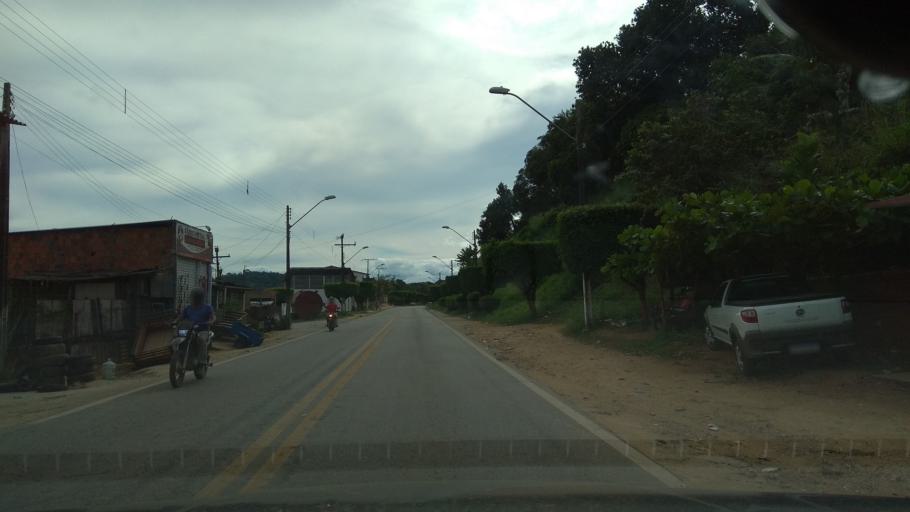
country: BR
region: Bahia
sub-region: Ubata
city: Ubata
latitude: -14.2093
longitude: -39.5260
